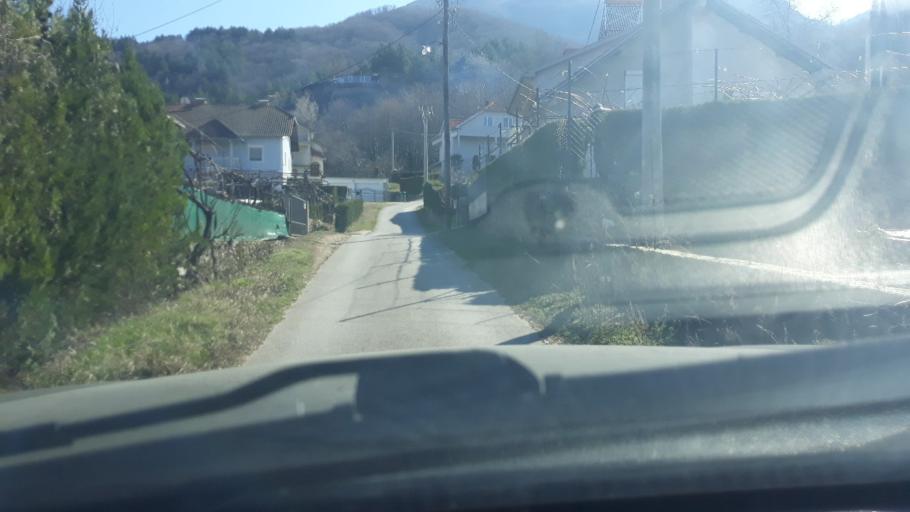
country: MK
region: Bosilovo
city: Sekirnik
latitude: 41.3791
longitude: 22.8120
